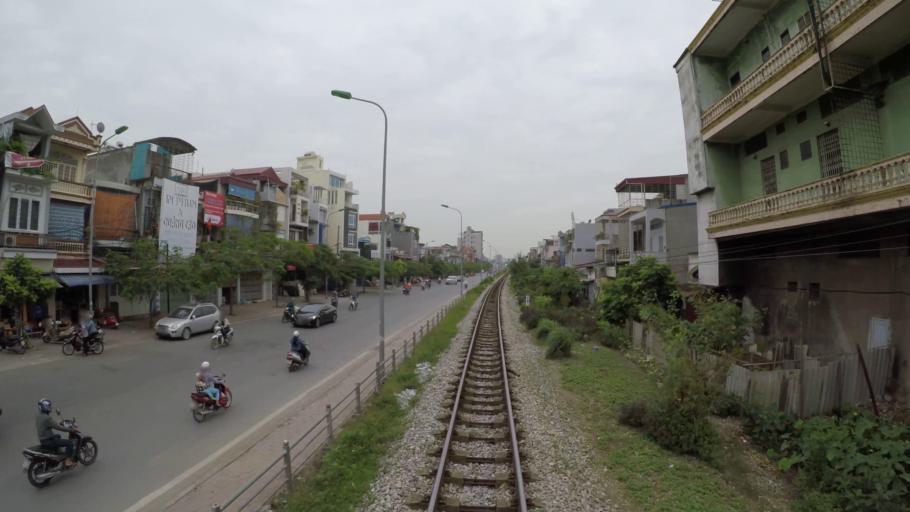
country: VN
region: Hai Phong
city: An Duong
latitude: 20.8740
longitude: 106.6421
